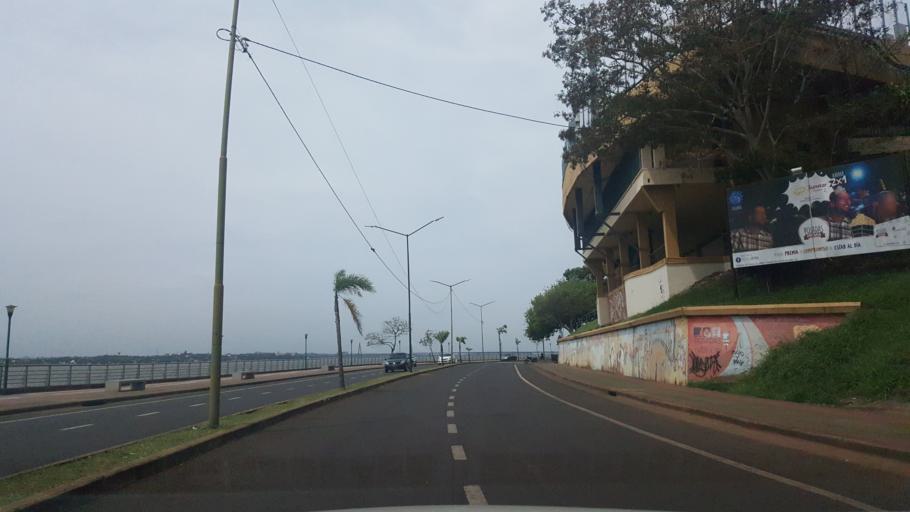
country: AR
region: Misiones
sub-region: Departamento de Capital
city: Posadas
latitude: -27.3530
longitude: -55.8937
